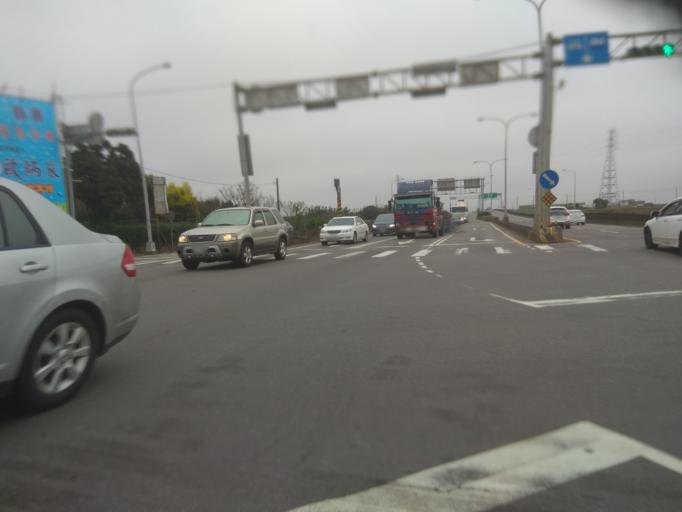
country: TW
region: Taiwan
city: Taoyuan City
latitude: 24.9931
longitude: 121.1117
